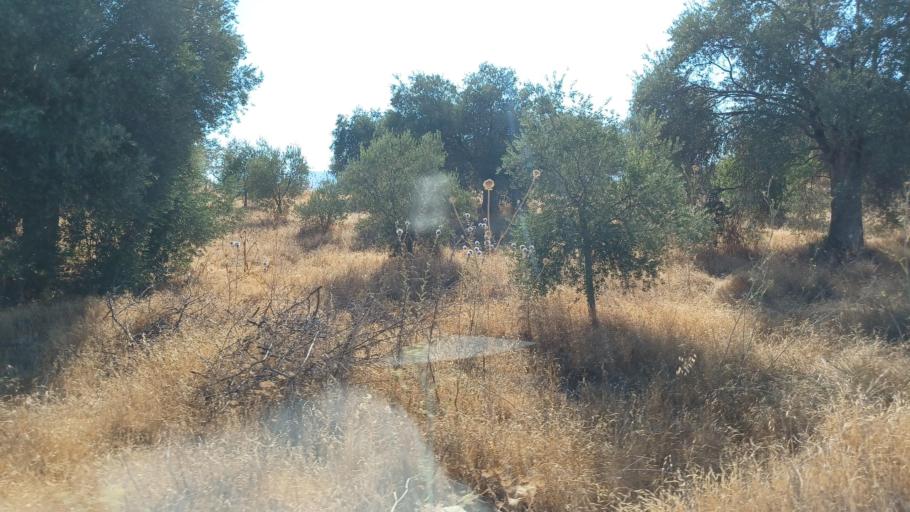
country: CY
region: Limassol
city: Pachna
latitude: 34.8482
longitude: 32.7107
